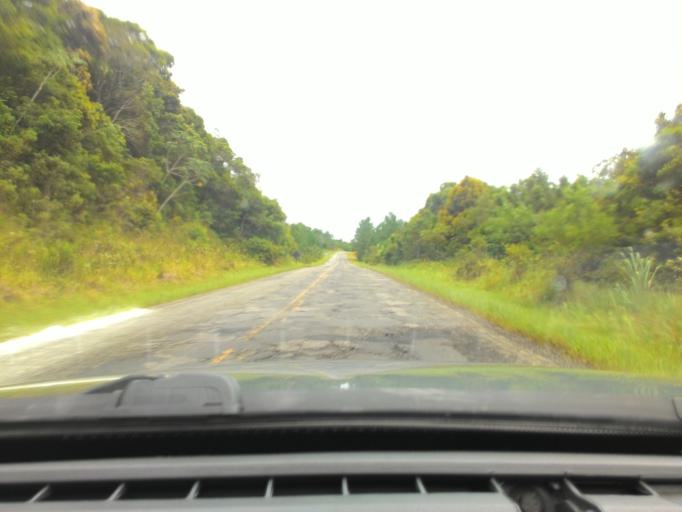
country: BR
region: Sao Paulo
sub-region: Pariquera-Acu
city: Pariquera Acu
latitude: -24.7535
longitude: -47.7919
